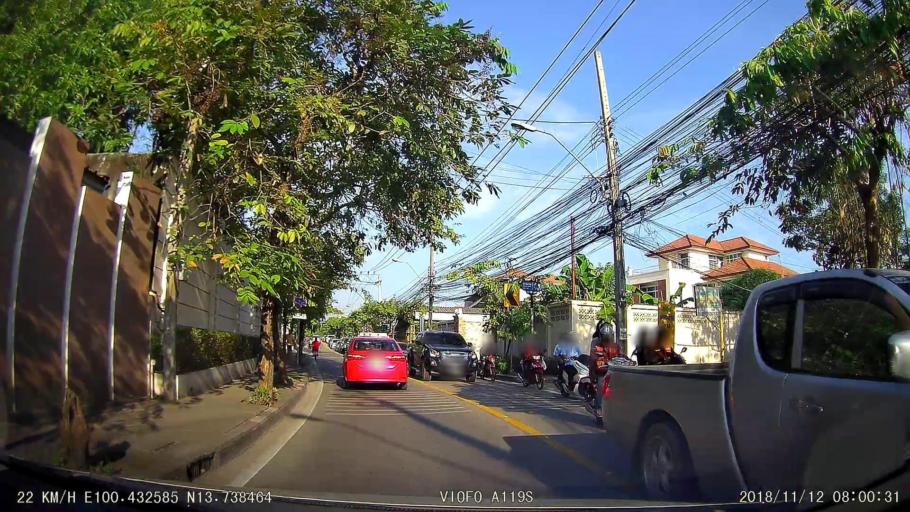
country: TH
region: Bangkok
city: Phasi Charoen
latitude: 13.7385
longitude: 100.4326
